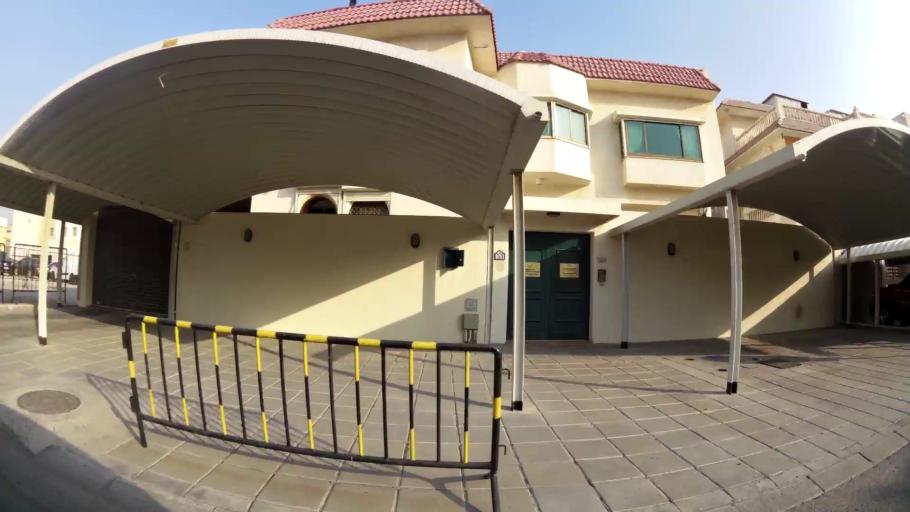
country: KW
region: Muhafazat Hawalli
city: Salwa
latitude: 29.3042
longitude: 48.0800
